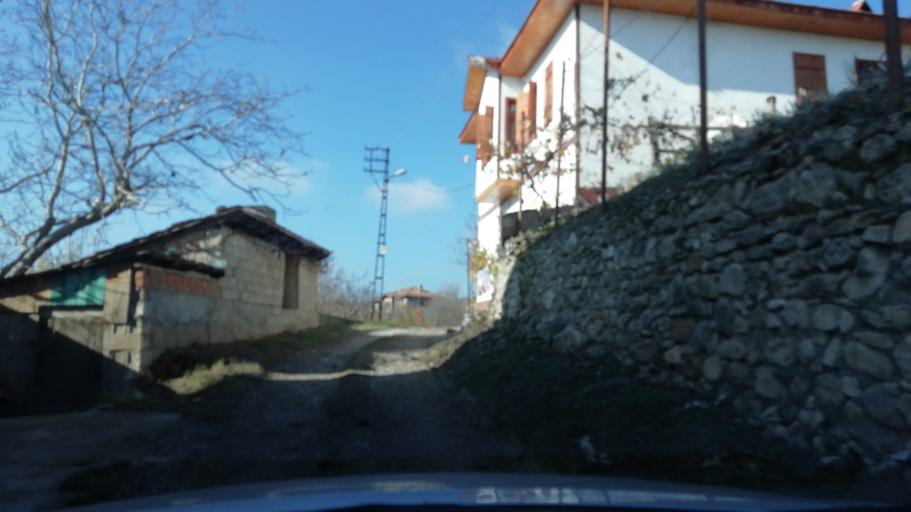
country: TR
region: Karabuk
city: Safranbolu
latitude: 41.2330
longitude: 32.7833
